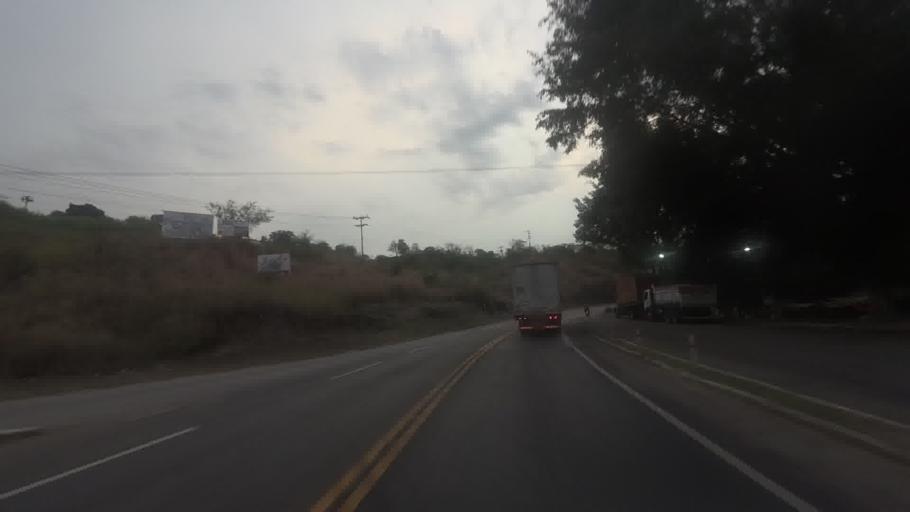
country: BR
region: Minas Gerais
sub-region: Alem Paraiba
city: Alem Paraiba
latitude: -21.8770
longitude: -42.6677
